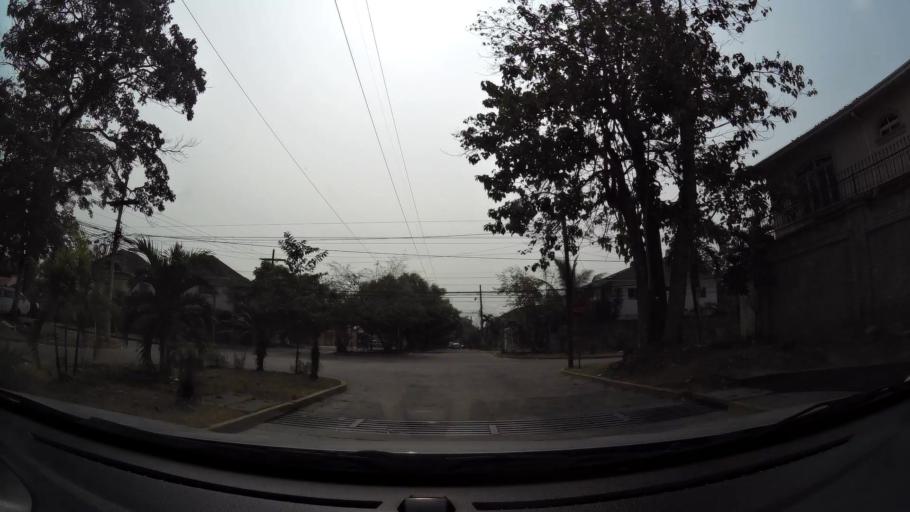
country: HN
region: Cortes
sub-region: San Pedro Sula
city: Pena Blanca
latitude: 15.5382
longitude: -88.0330
